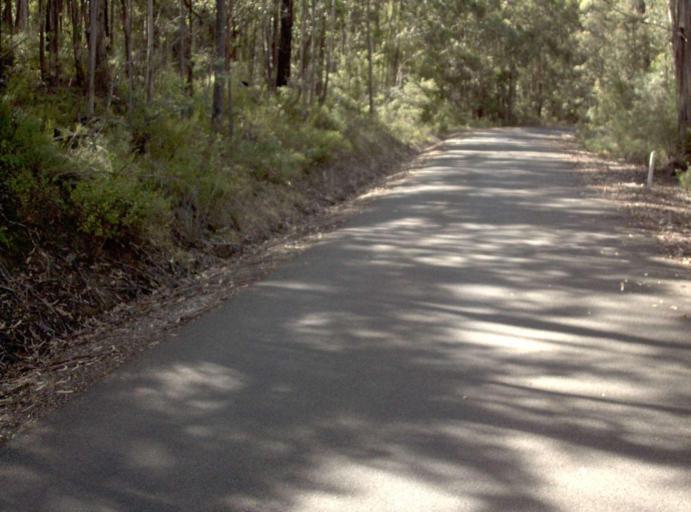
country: AU
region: Victoria
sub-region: East Gippsland
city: Lakes Entrance
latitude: -37.4375
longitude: 148.1325
